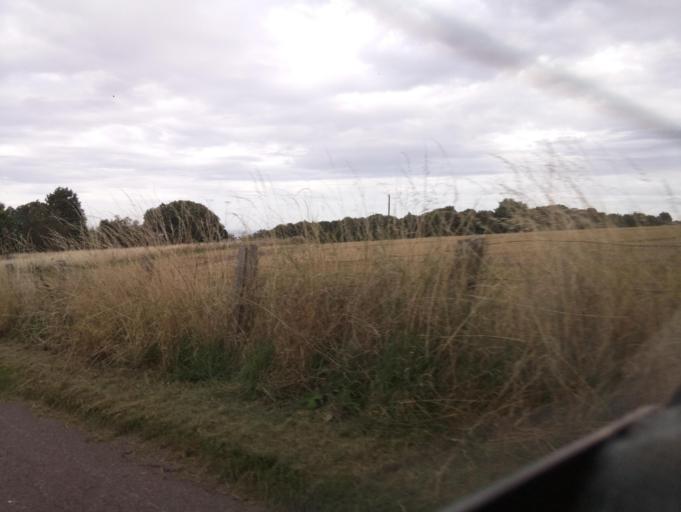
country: GB
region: Scotland
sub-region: Fife
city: Saint Andrews
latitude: 56.3195
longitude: -2.7799
